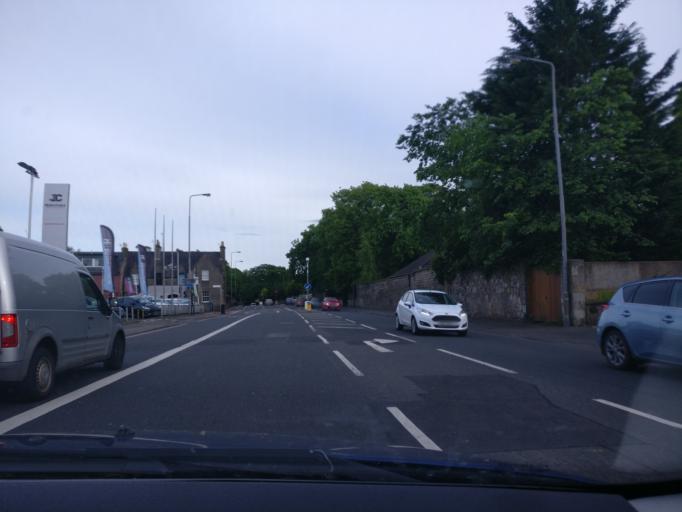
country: GB
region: Scotland
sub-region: West Lothian
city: Seafield
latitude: 55.9466
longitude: -3.1365
